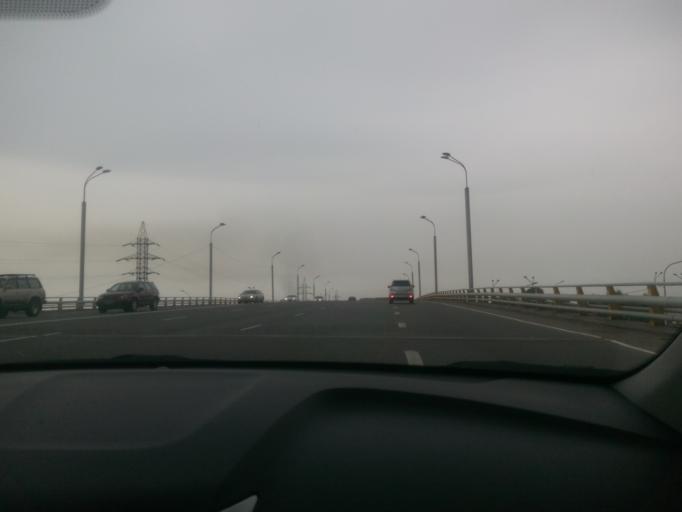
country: KZ
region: Almaty Qalasy
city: Almaty
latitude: 43.2426
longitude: 76.8282
